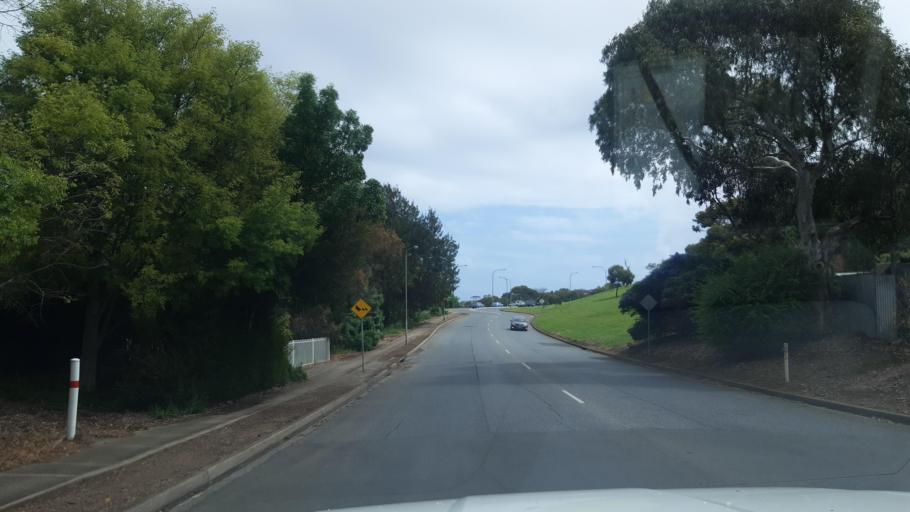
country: AU
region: South Australia
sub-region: Marion
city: Happy Valley
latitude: -35.0766
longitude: 138.5346
